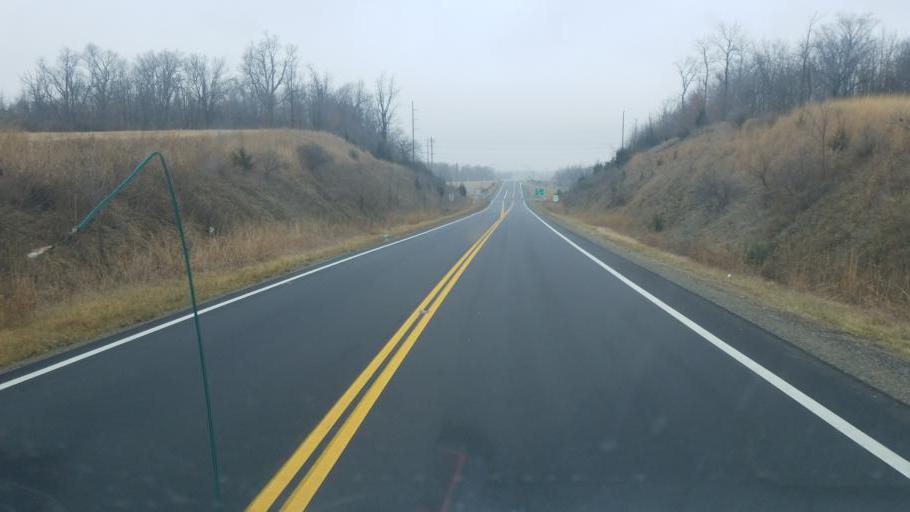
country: US
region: Ohio
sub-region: Champaign County
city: North Lewisburg
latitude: 40.3202
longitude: -83.5936
